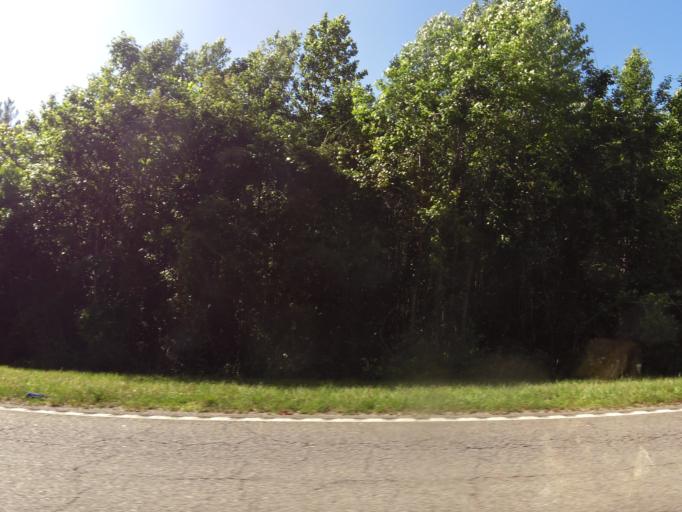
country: US
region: South Carolina
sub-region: Allendale County
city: Allendale
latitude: 33.1060
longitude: -81.1922
